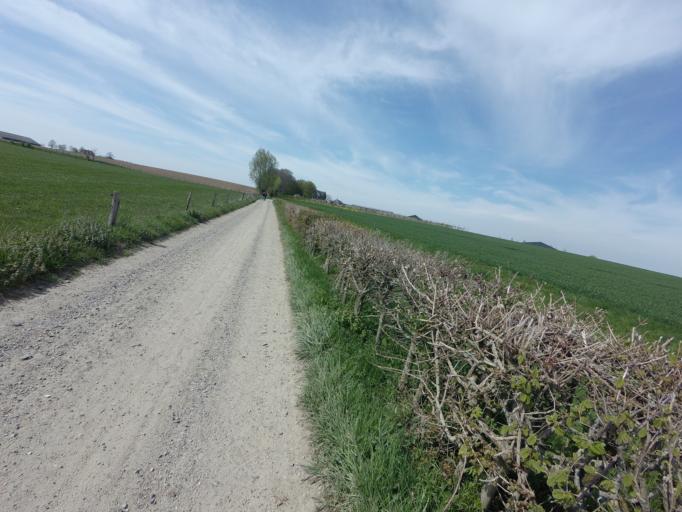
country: NL
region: Limburg
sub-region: Eijsden-Margraten
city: Margraten
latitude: 50.7932
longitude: 5.8250
